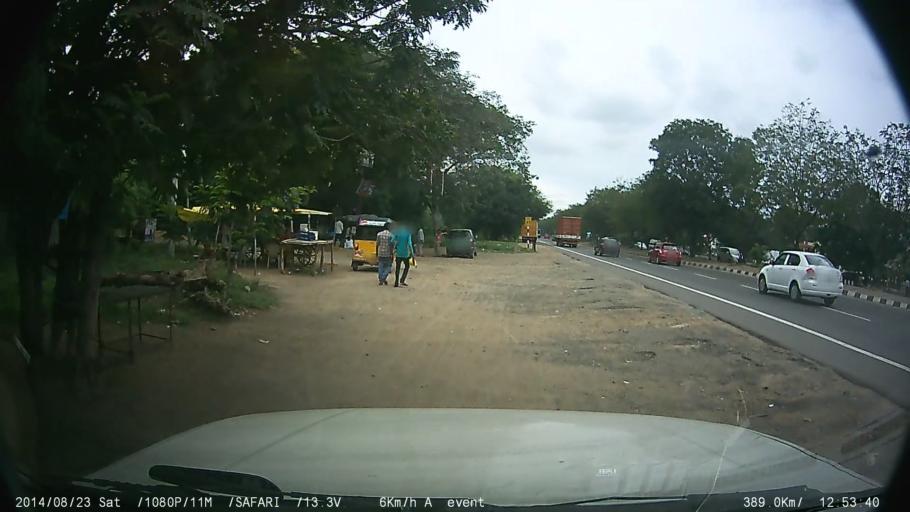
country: IN
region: Tamil Nadu
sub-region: Kancheepuram
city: Singapperumalkovil
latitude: 12.7959
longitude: 80.0205
